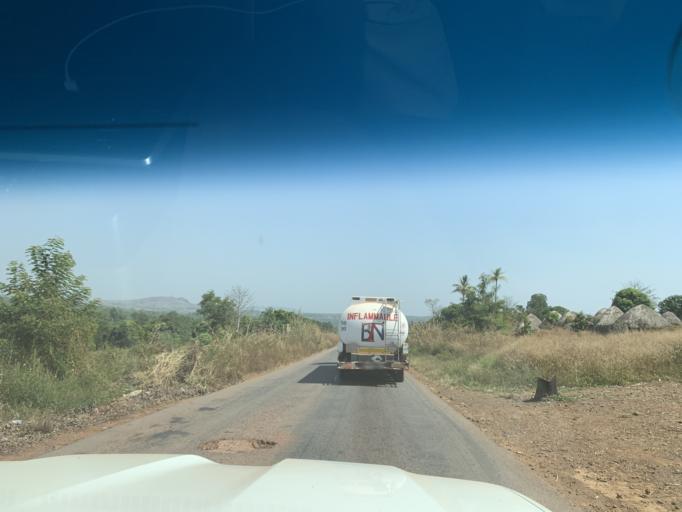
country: GN
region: Kindia
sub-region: Kindia
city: Kindia
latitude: 9.9981
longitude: -12.7119
